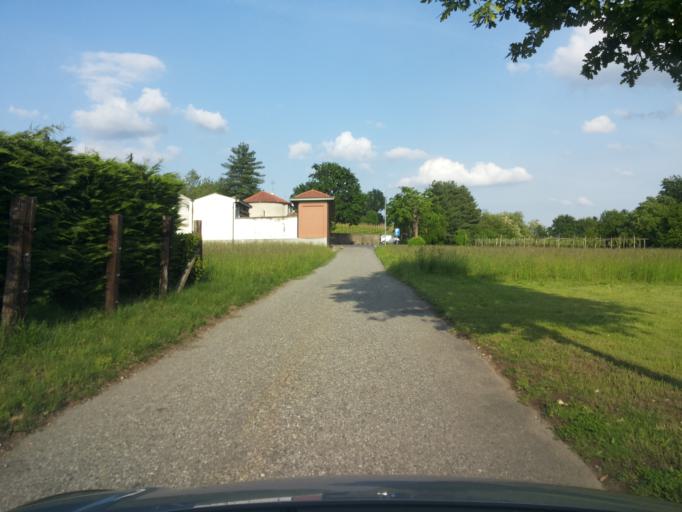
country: IT
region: Piedmont
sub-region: Provincia di Torino
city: Azeglio
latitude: 45.4261
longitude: 7.9840
